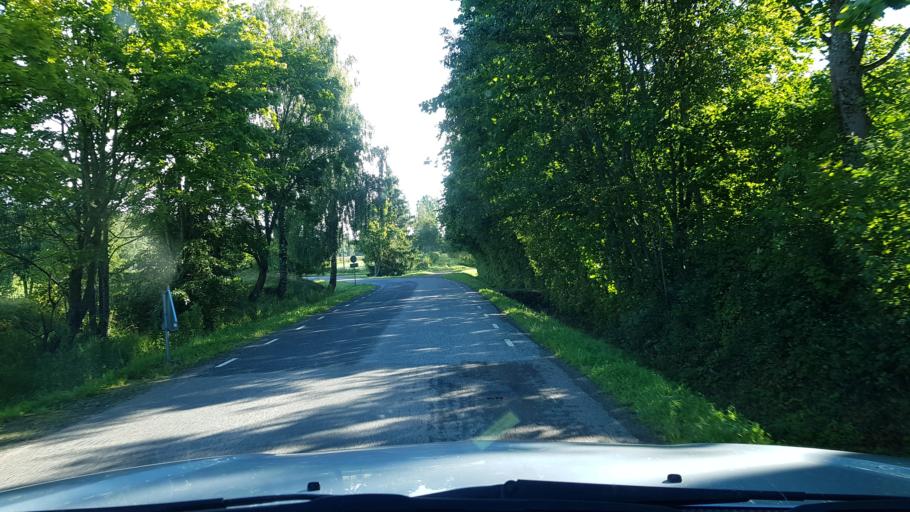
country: EE
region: Harju
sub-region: Rae vald
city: Vaida
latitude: 59.3025
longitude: 24.9253
